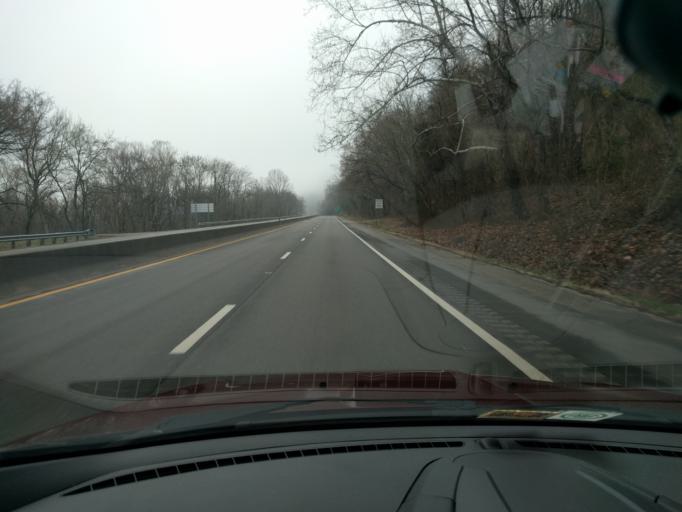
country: US
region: West Virginia
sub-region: Kanawha County
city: Rand
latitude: 38.2935
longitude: -81.5584
